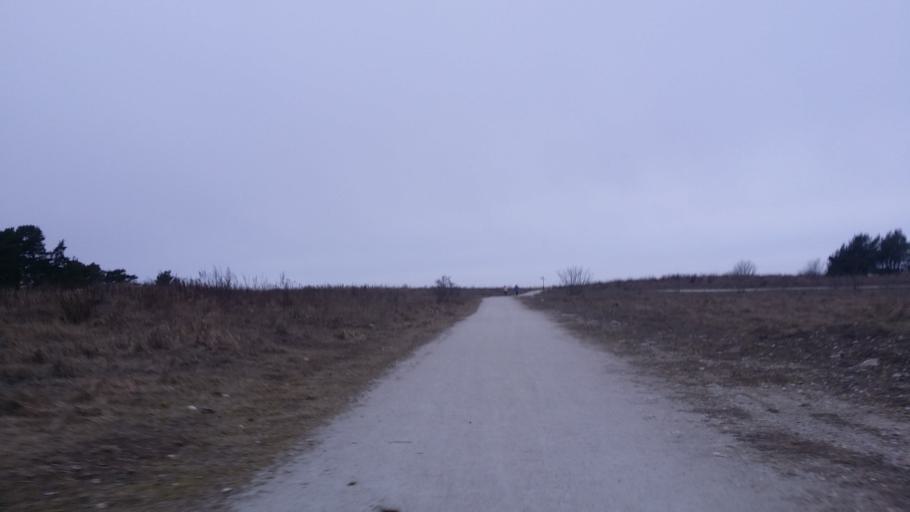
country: SE
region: Gotland
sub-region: Gotland
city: Vibble
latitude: 57.6176
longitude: 18.2645
